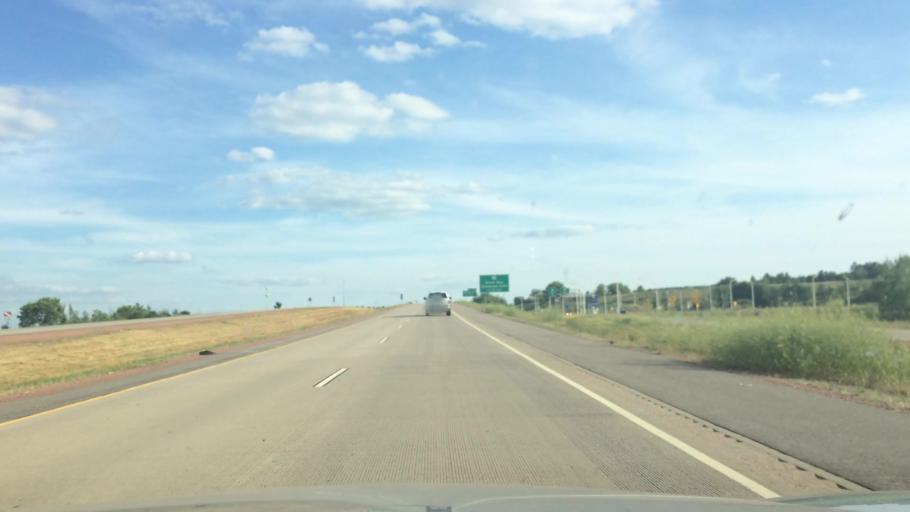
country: US
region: Wisconsin
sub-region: Marathon County
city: Wausau
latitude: 44.9944
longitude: -89.6575
